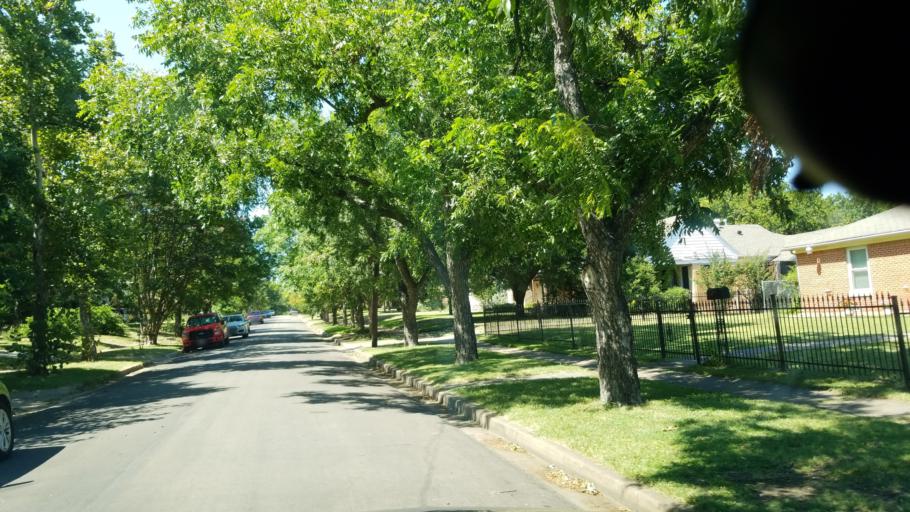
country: US
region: Texas
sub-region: Dallas County
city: Cockrell Hill
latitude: 32.7267
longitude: -96.8556
